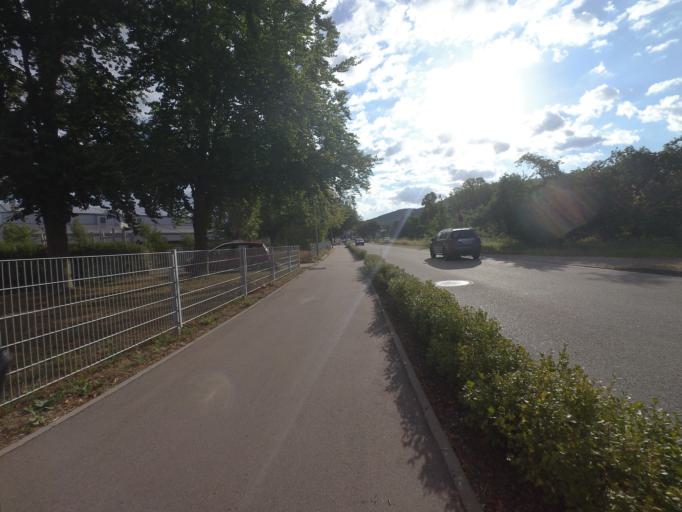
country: DE
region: Baden-Wuerttemberg
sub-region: Karlsruhe Region
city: Sinzheim
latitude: 48.7552
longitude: 8.1636
